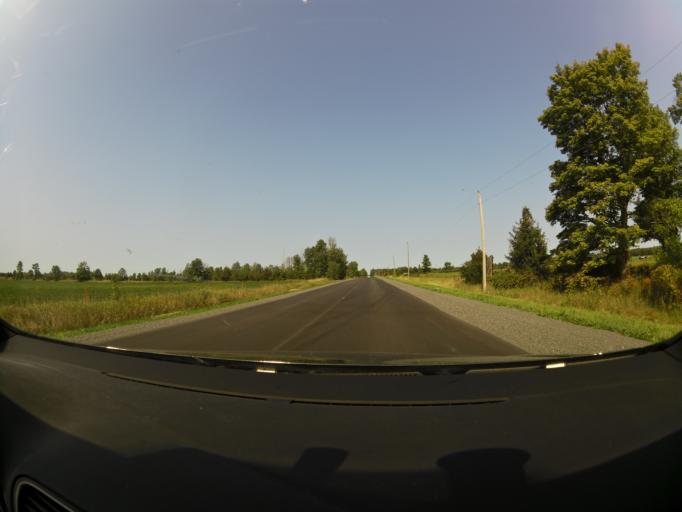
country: CA
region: Ontario
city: Arnprior
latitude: 45.4809
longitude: -76.1810
